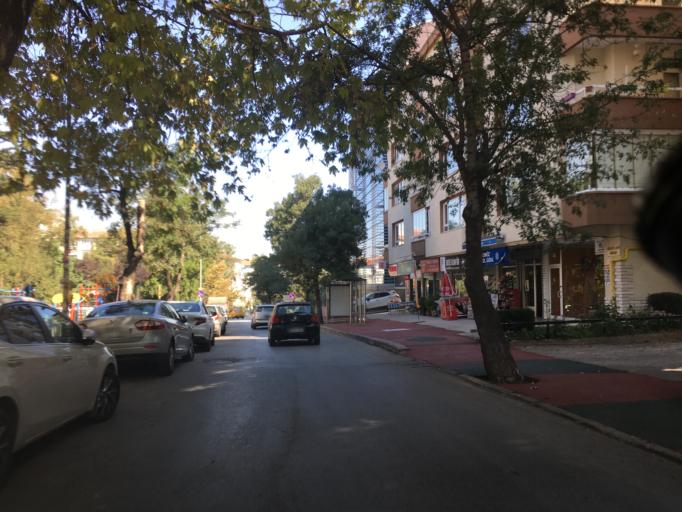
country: TR
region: Ankara
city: Ankara
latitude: 39.8987
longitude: 32.8506
